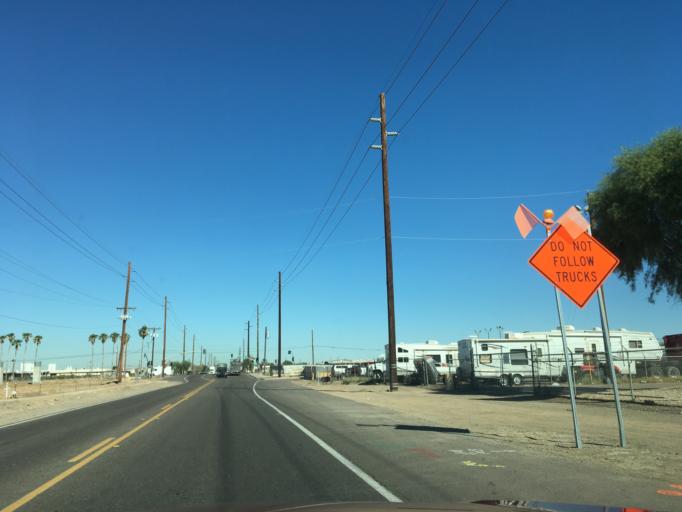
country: US
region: Arizona
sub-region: Maricopa County
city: Laveen
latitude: 33.4351
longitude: -112.1865
